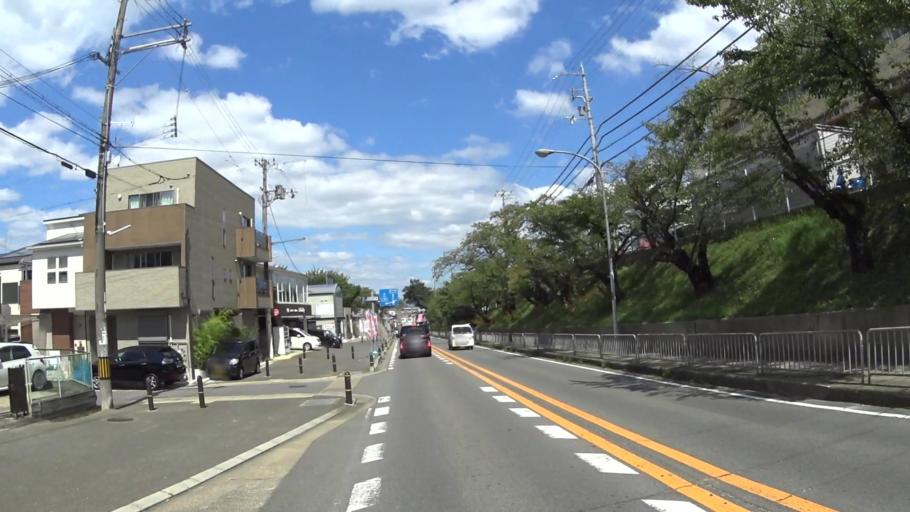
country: JP
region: Kyoto
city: Uji
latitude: 34.8874
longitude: 135.7818
